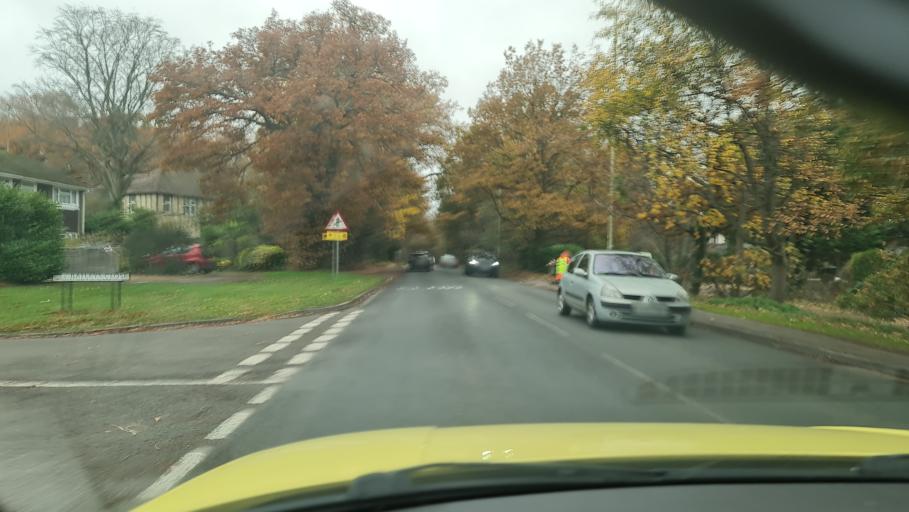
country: GB
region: England
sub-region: Bracknell Forest
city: Sandhurst
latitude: 51.3315
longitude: -0.7949
